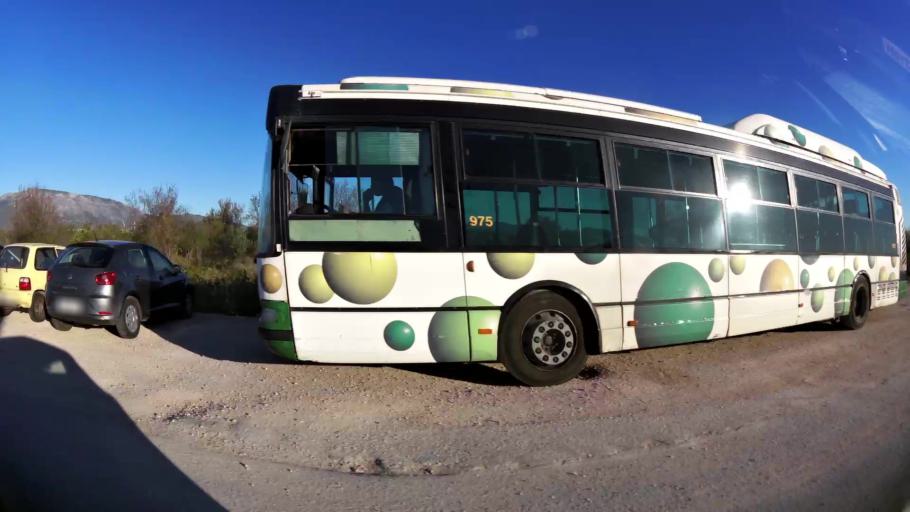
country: GR
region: Attica
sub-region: Nomarchia Anatolikis Attikis
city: Koropi
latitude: 37.9141
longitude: 23.8997
